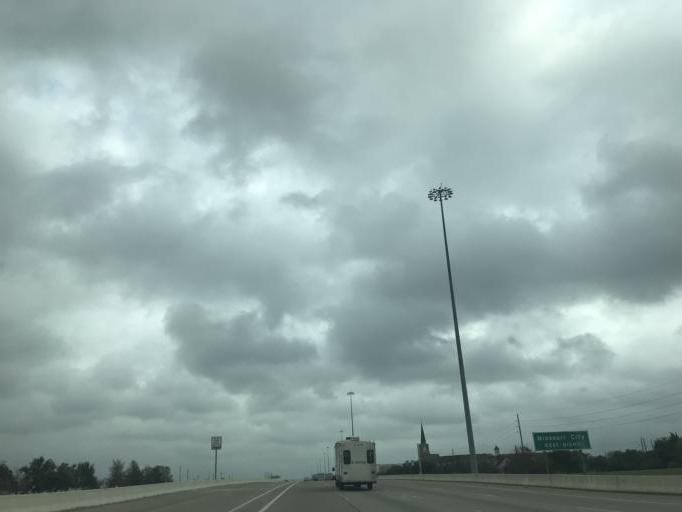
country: US
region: Texas
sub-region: Fort Bend County
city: Sugar Land
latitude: 29.5847
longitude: -95.6421
